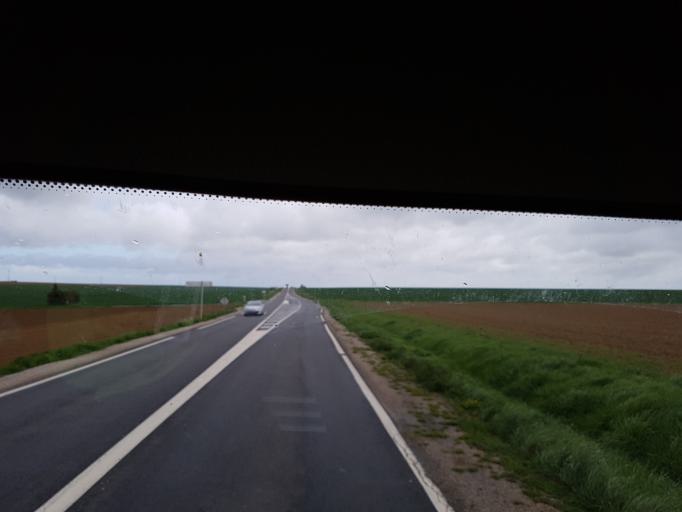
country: FR
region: Picardie
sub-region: Departement de l'Aisne
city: Crouy
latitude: 49.4498
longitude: 3.3570
